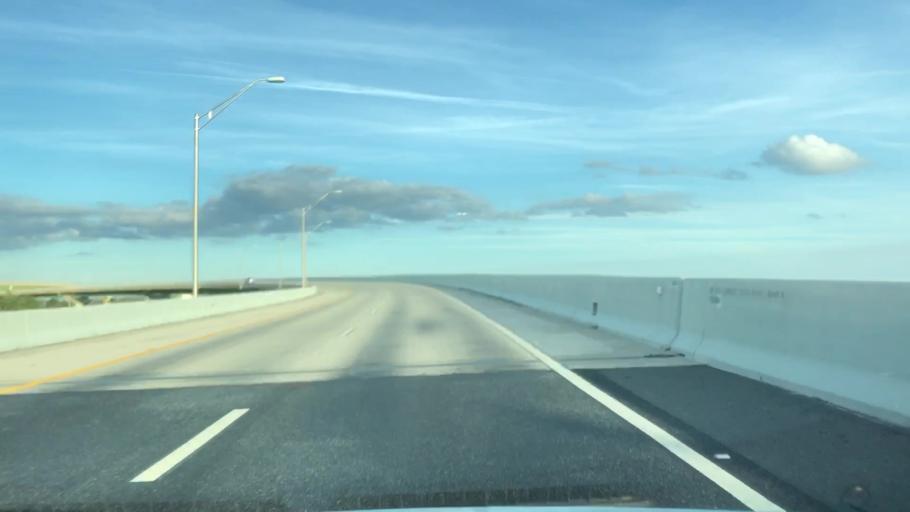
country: US
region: Florida
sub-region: Osceola County
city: Buenaventura Lakes
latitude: 28.3675
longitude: -81.3127
